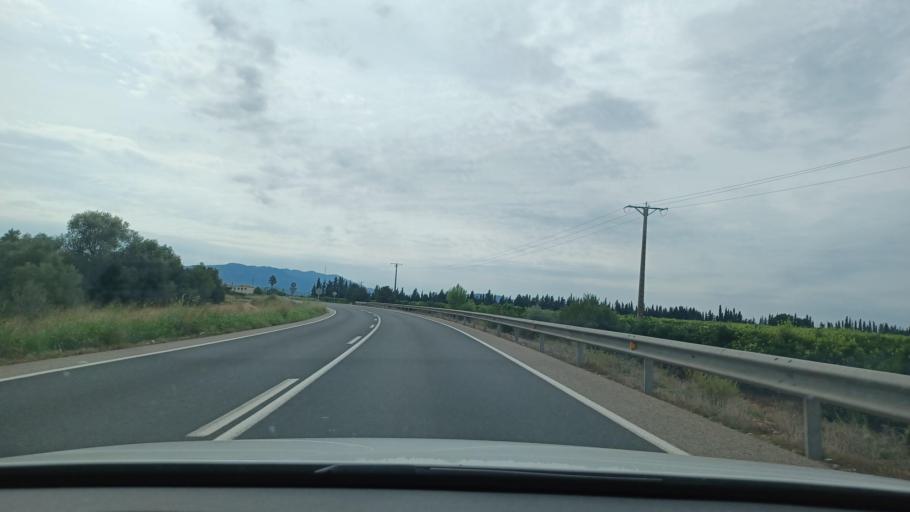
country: ES
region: Catalonia
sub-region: Provincia de Tarragona
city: Santa Barbara
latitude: 40.7567
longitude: 0.5017
